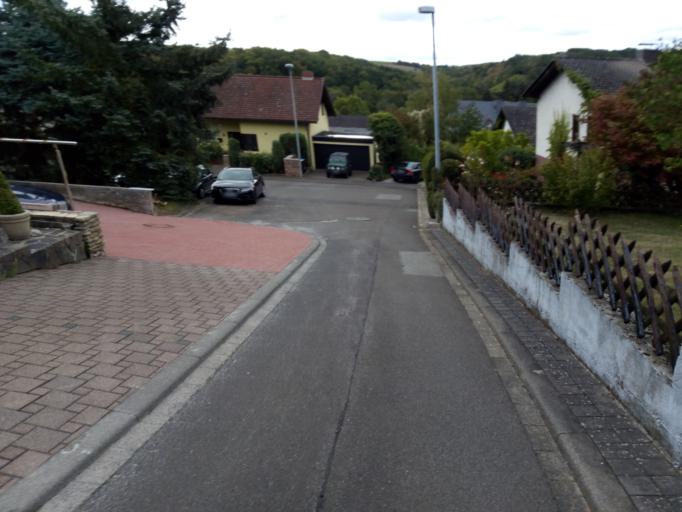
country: DE
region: Rheinland-Pfalz
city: Schweppenhausen
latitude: 49.9240
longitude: 7.8036
